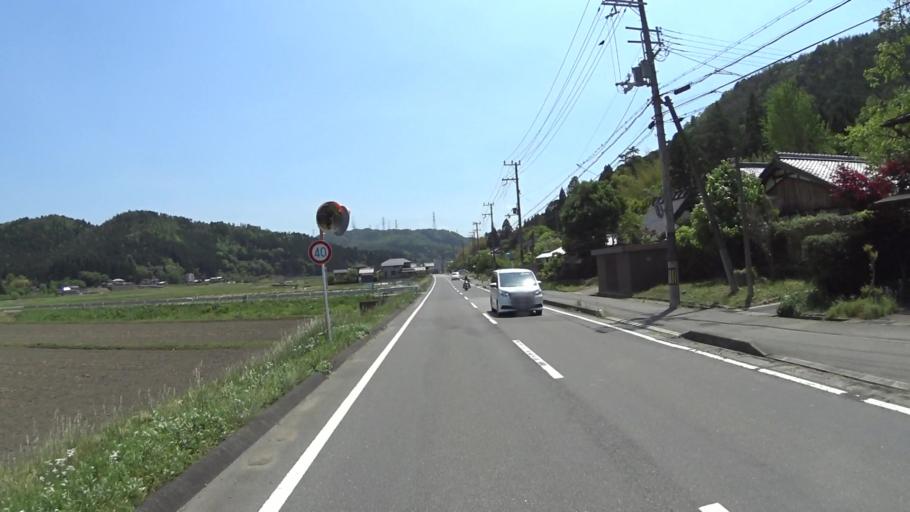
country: JP
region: Kyoto
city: Kameoka
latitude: 35.0194
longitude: 135.4874
